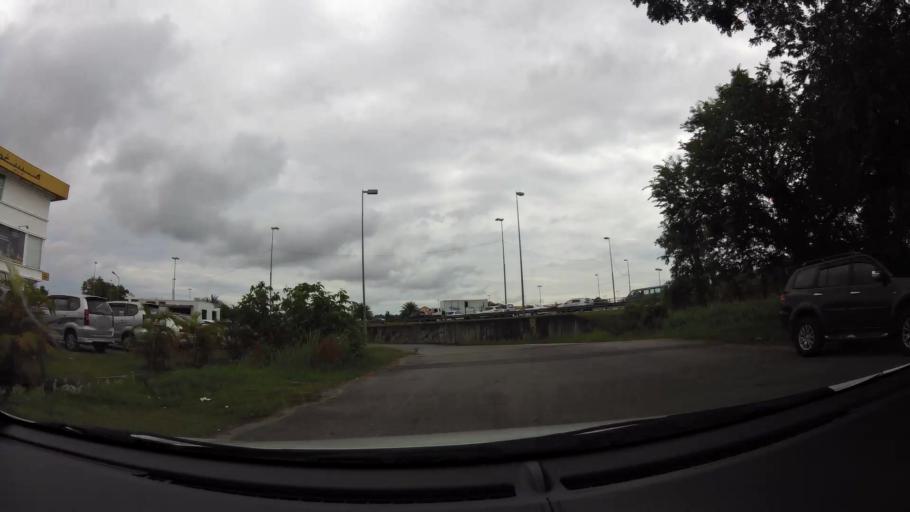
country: BN
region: Brunei and Muara
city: Bandar Seri Begawan
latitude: 4.8995
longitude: 114.9190
